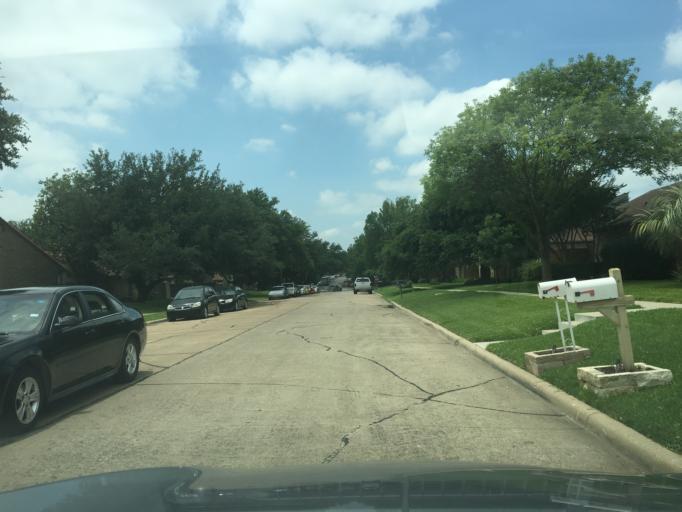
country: US
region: Texas
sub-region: Dallas County
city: Richardson
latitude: 32.9452
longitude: -96.7622
